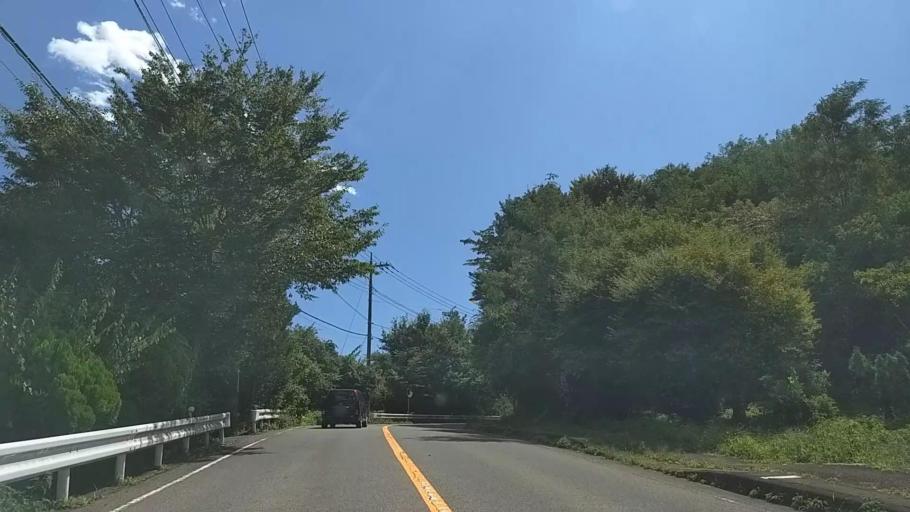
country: JP
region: Tokyo
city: Hachioji
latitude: 35.5693
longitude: 139.2817
